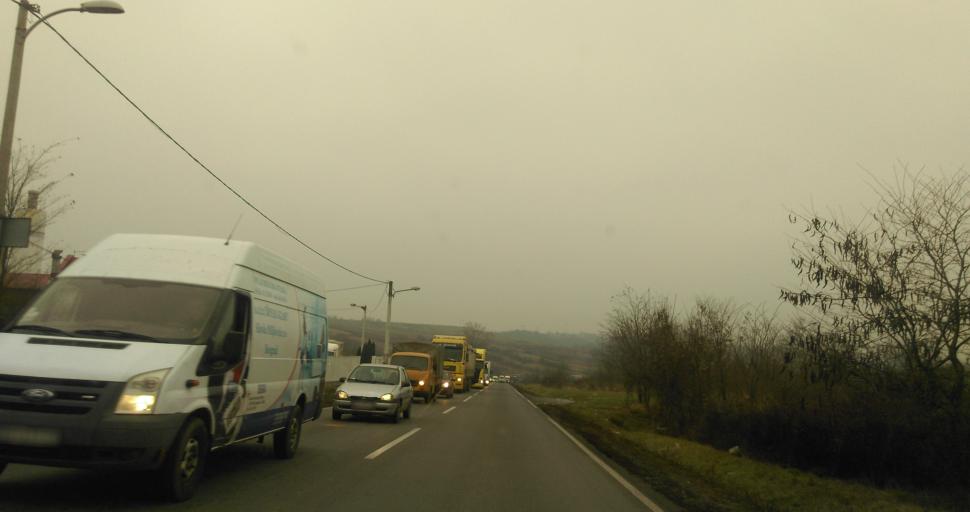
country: RS
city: Rusanj
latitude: 44.7151
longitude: 20.4886
